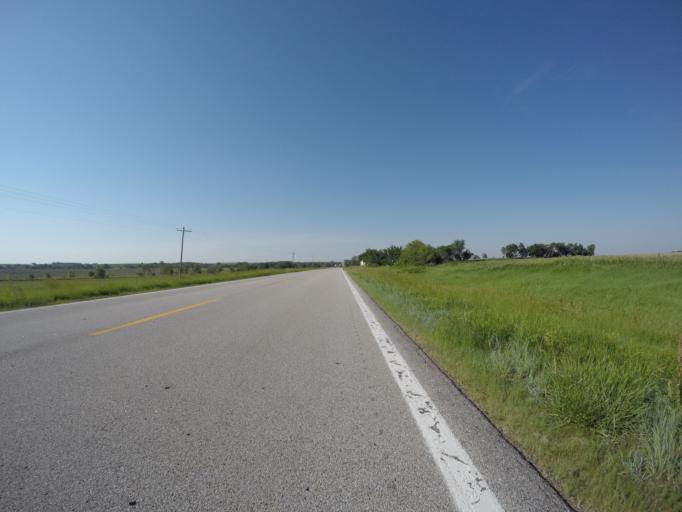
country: US
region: Nebraska
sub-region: Gage County
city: Wymore
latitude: 40.0509
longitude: -96.4828
